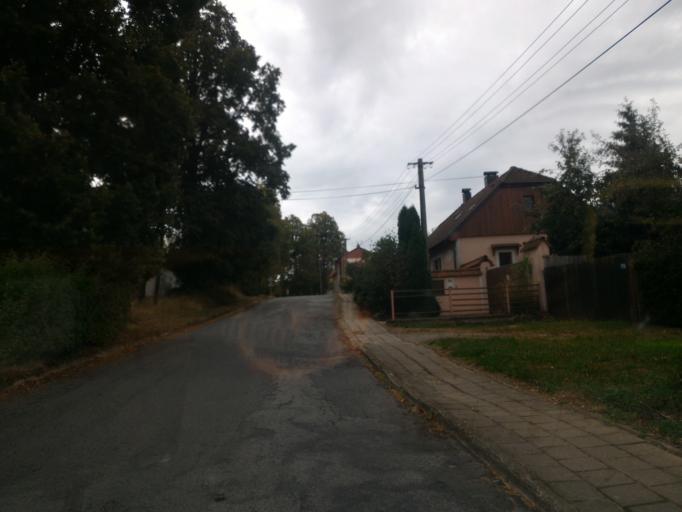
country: CZ
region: Jihocesky
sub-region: Okres Jindrichuv Hradec
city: Dacice
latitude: 49.1074
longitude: 15.4221
